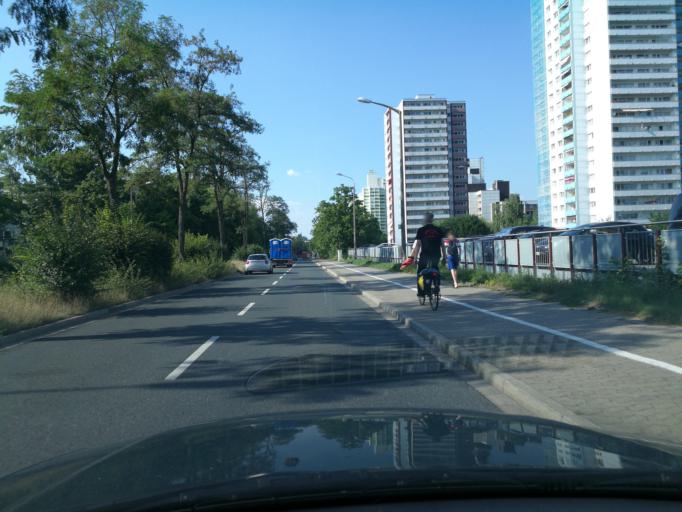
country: DE
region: Bavaria
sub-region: Regierungsbezirk Mittelfranken
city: Erlangen
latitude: 49.5903
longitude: 10.9698
